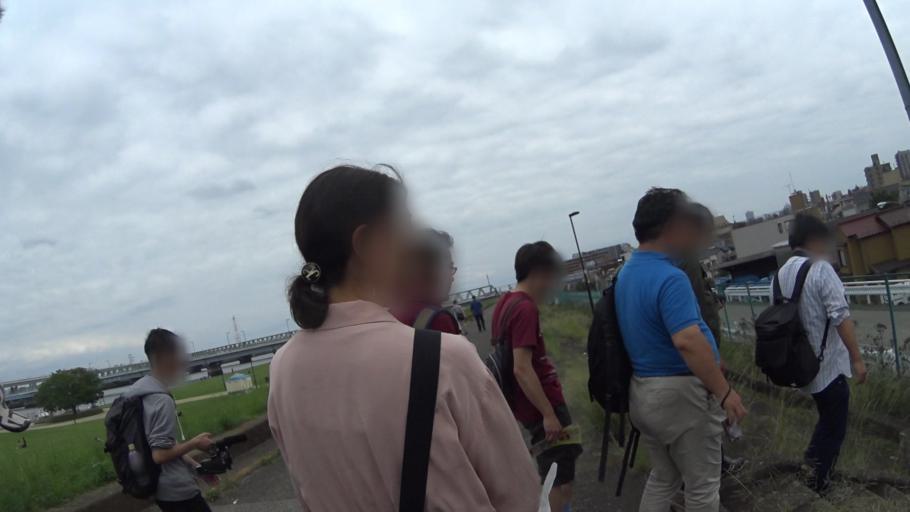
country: JP
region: Tokyo
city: Urayasu
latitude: 35.7135
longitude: 139.8444
